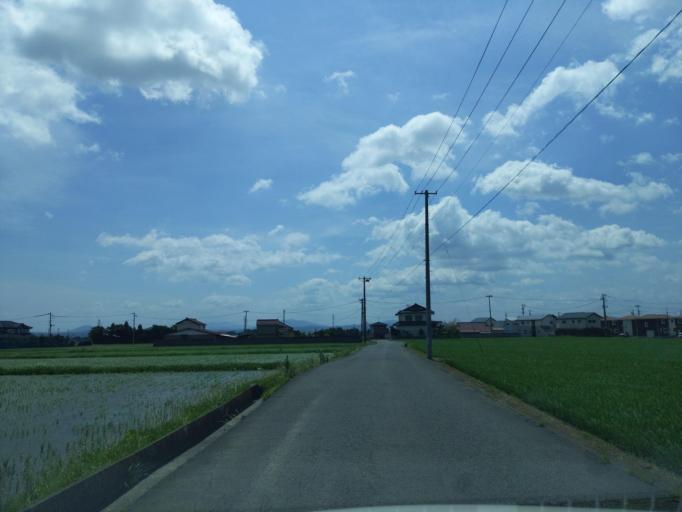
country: JP
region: Fukushima
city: Koriyama
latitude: 37.4376
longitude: 140.3516
